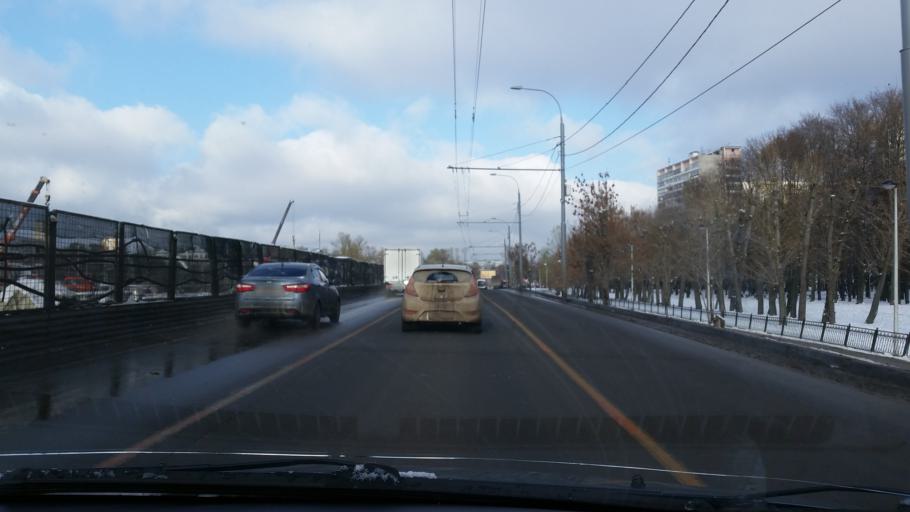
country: RU
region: Moscow
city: Zapadnoye Degunino
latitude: 55.8660
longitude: 37.5478
